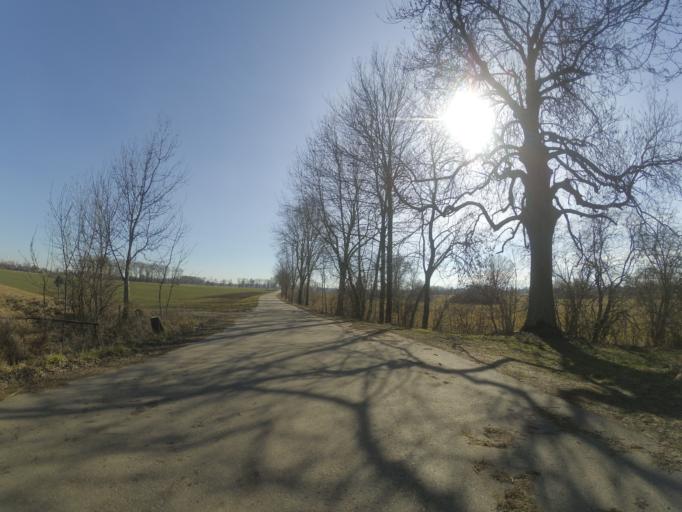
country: DE
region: Baden-Wuerttemberg
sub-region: Tuebingen Region
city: Rammingen
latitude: 48.5009
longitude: 10.1511
